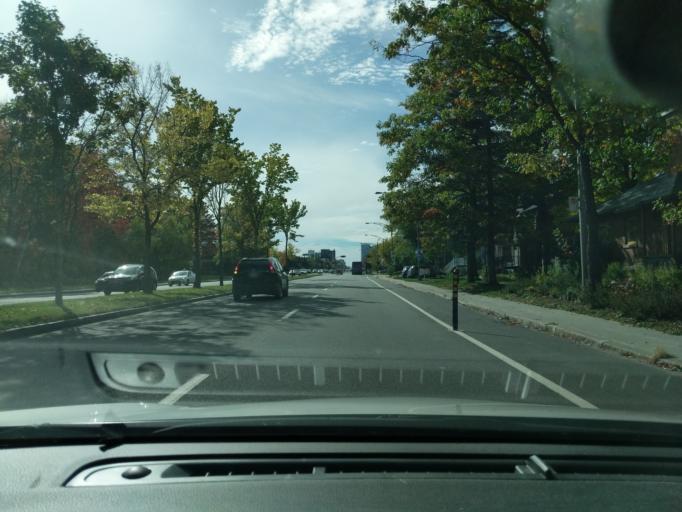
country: CA
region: Quebec
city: Quebec
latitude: 46.7804
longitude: -71.2630
